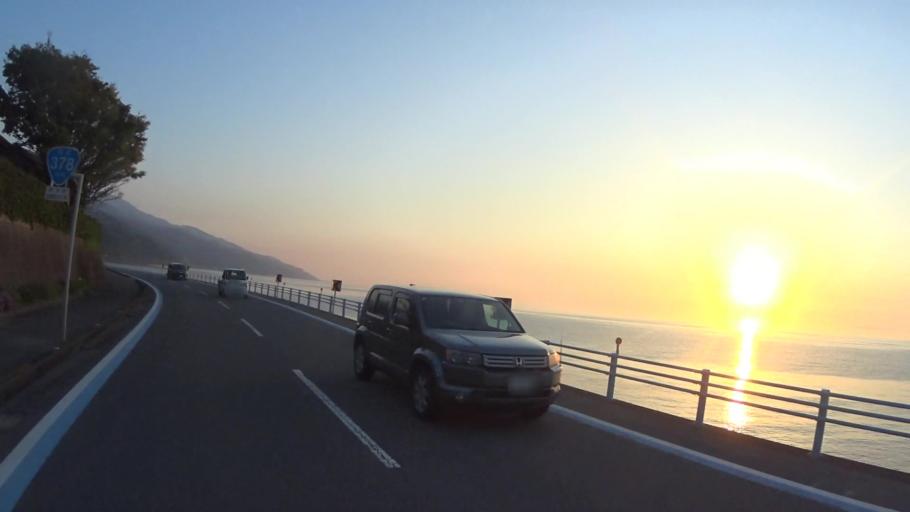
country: JP
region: Ehime
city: Iyo
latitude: 33.6729
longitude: 132.6128
